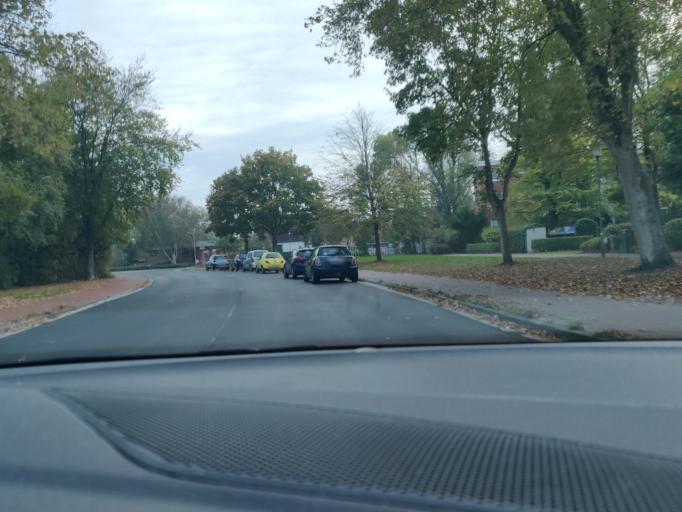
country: DE
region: Lower Saxony
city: Cuxhaven
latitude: 53.8854
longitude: 8.6743
